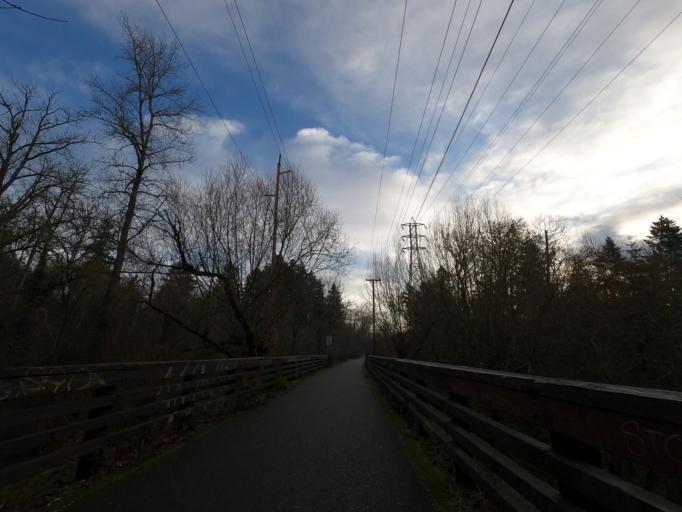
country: US
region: Oregon
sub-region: Clackamas County
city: Milwaukie
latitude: 45.4633
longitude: -122.6261
